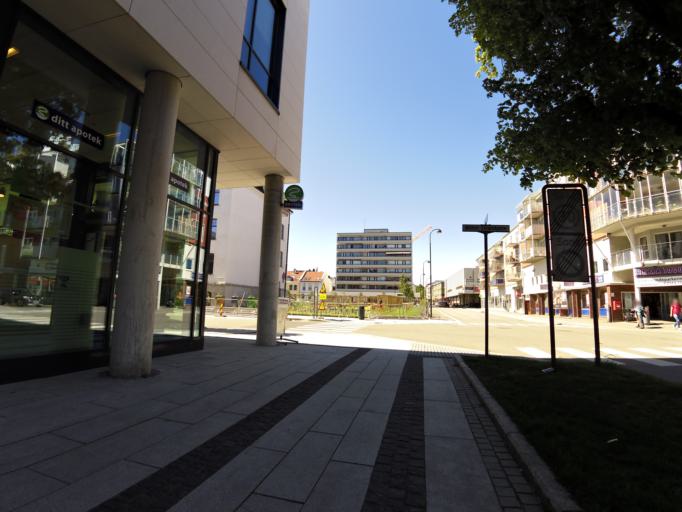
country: NO
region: Vest-Agder
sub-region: Kristiansand
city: Kristiansand
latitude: 58.1476
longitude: 8.0061
